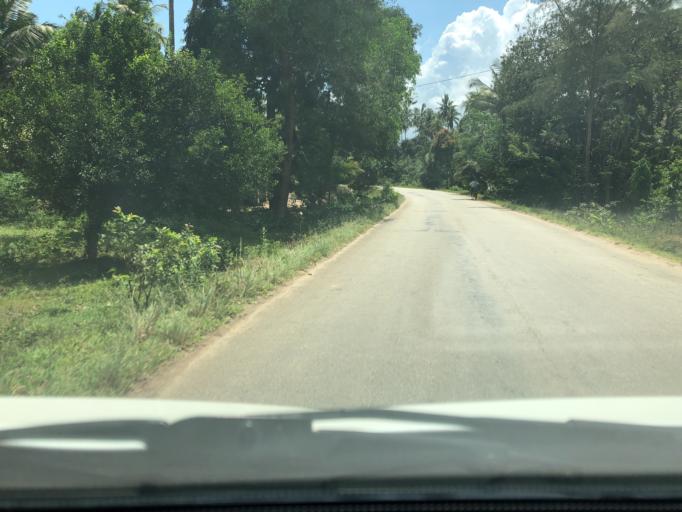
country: TZ
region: Zanzibar Central/South
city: Koani
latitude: -6.0515
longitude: 39.2530
